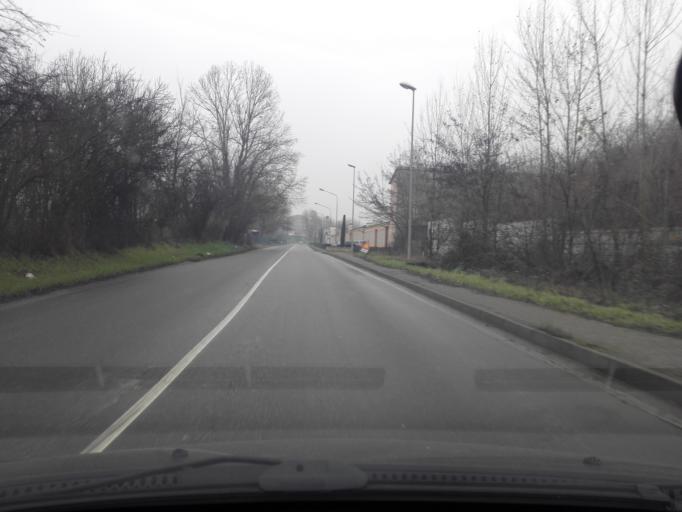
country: IT
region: Piedmont
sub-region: Provincia di Alessandria
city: Novi Ligure
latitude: 44.7692
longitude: 8.7758
